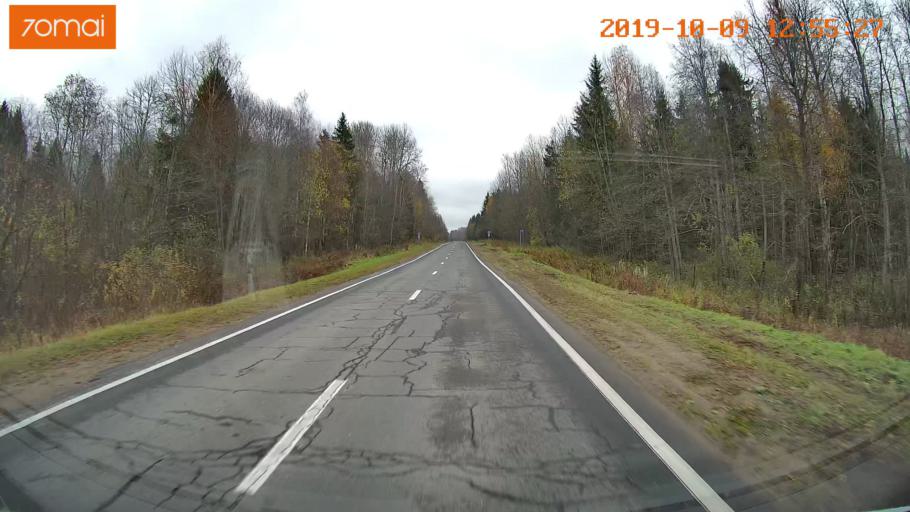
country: RU
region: Jaroslavl
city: Prechistoye
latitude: 58.3997
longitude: 40.3939
